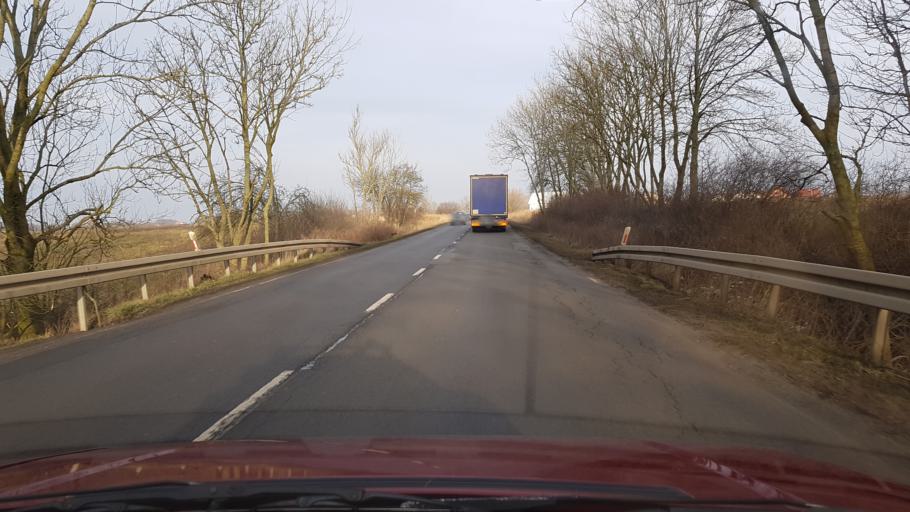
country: PL
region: West Pomeranian Voivodeship
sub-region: Powiat policki
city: Police
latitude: 53.5049
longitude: 14.5743
